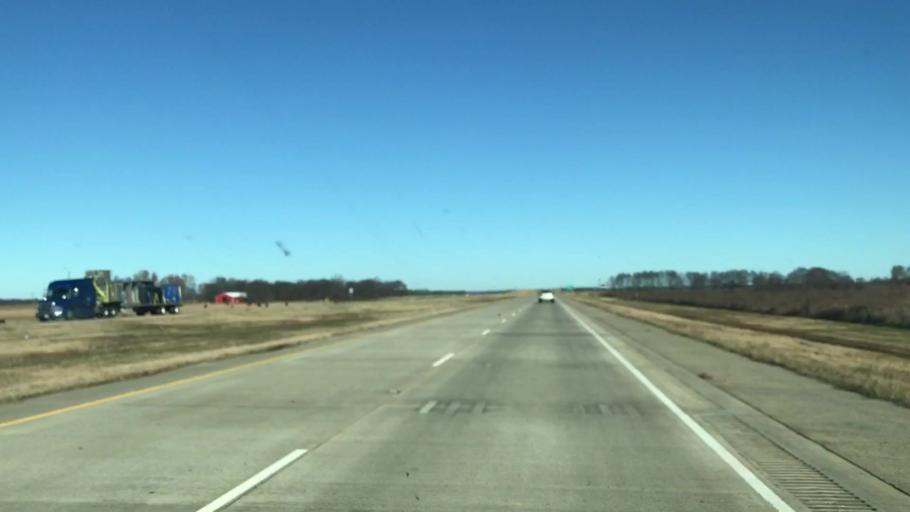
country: US
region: Louisiana
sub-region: Bossier Parish
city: Benton
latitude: 32.6913
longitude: -93.8568
